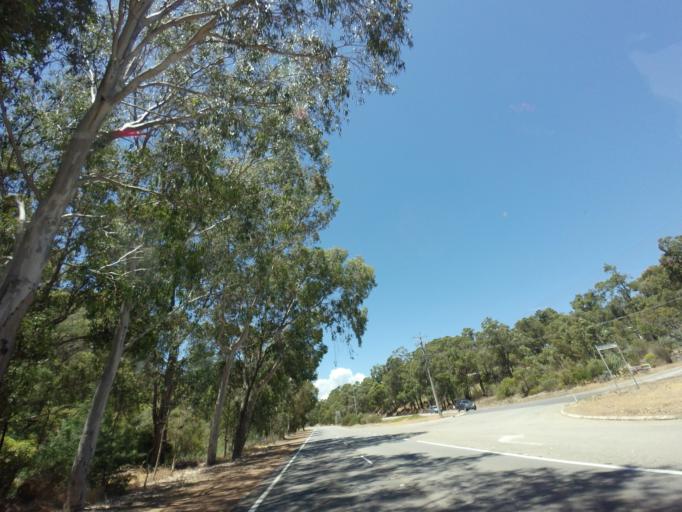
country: AU
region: Western Australia
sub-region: Mundaring
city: Parkerville
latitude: -31.8998
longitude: 116.1353
